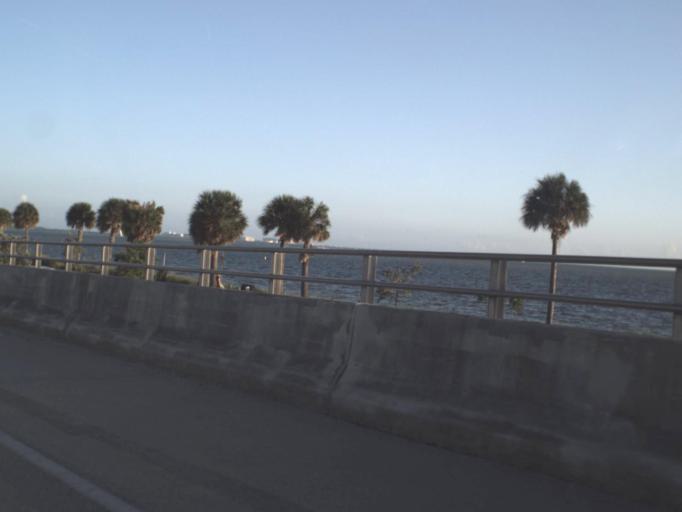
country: US
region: Florida
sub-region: Miami-Dade County
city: Miami
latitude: 25.7467
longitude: -80.2000
